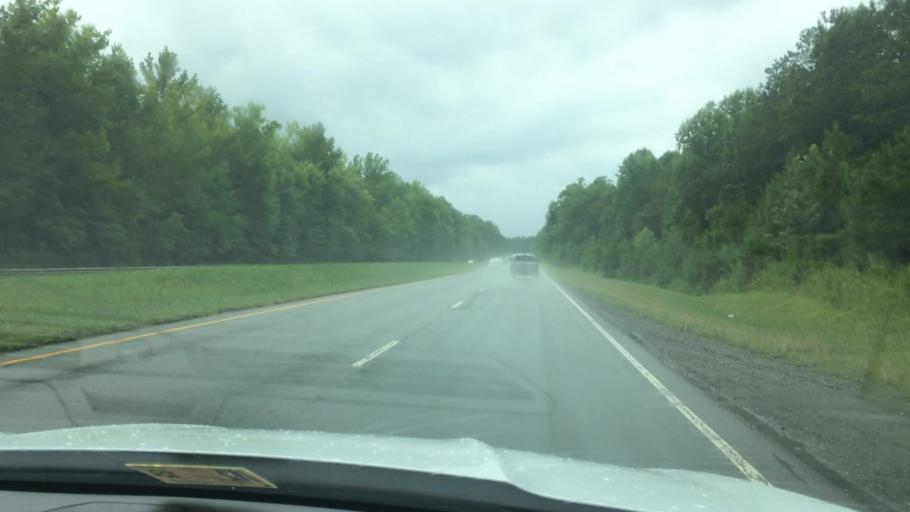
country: US
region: Virginia
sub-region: New Kent County
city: New Kent
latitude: 37.4967
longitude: -76.8866
